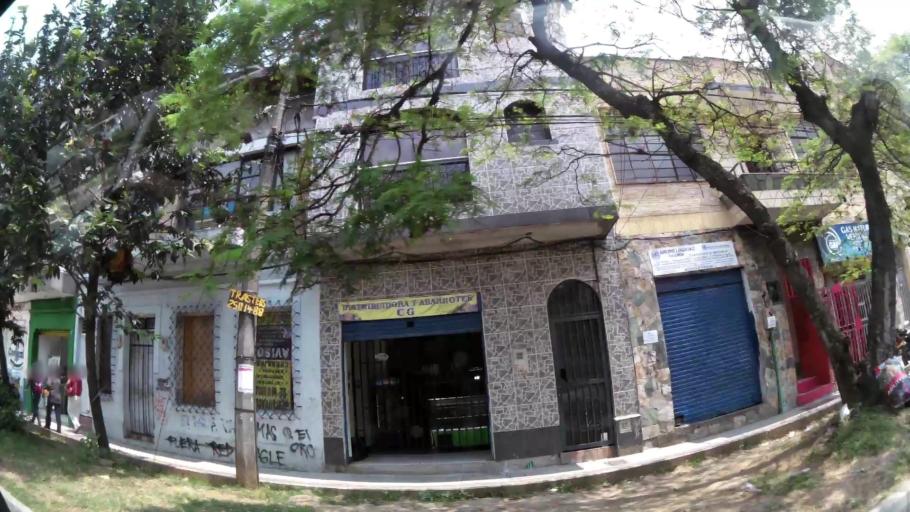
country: CO
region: Antioquia
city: Medellin
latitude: 6.2545
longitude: -75.5620
